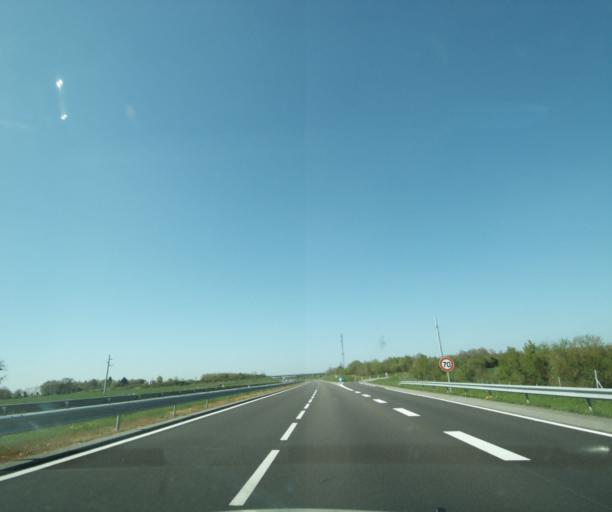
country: FR
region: Centre
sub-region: Departement du Loiret
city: Bonny-sur-Loire
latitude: 47.5680
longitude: 2.8781
